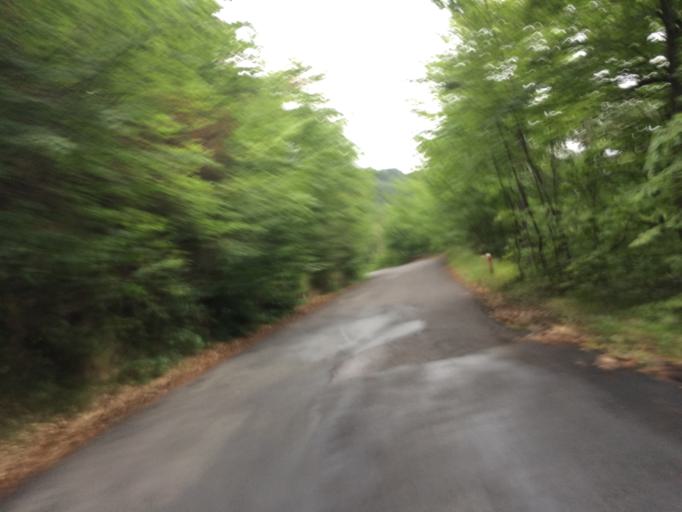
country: IT
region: Liguria
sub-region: Provincia di Imperia
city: Triora
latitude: 43.9769
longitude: 7.7465
